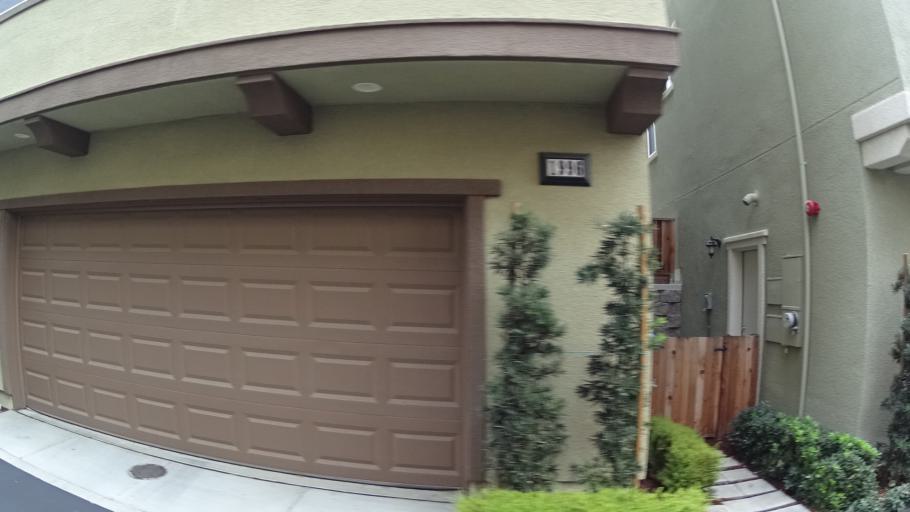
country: US
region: California
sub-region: Santa Clara County
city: Burbank
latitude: 37.3259
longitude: -121.9525
